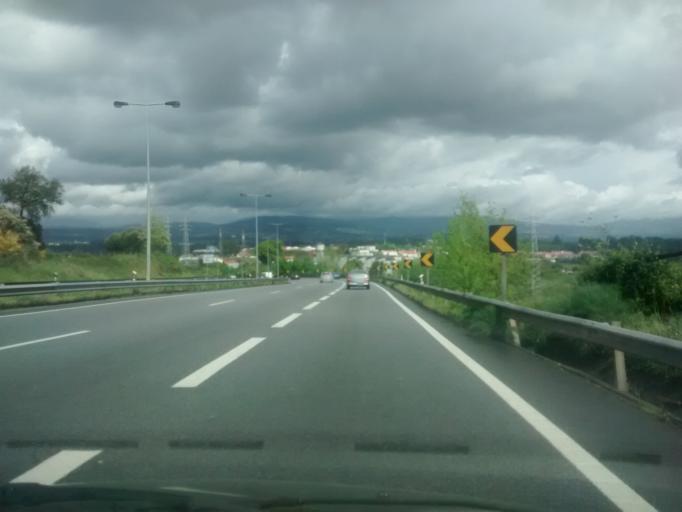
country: PT
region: Braga
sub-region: Braga
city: Braga
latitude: 41.5677
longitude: -8.4214
